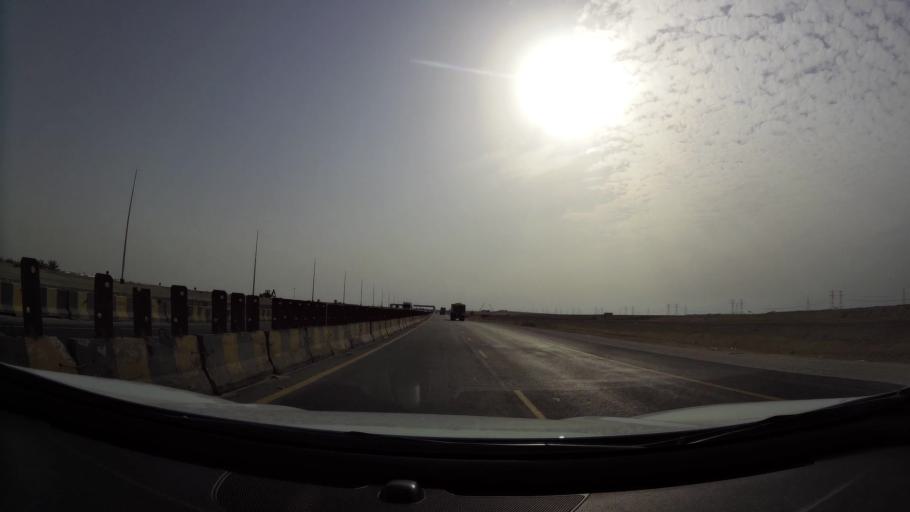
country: AE
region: Abu Dhabi
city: Abu Dhabi
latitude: 24.2543
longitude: 54.4807
